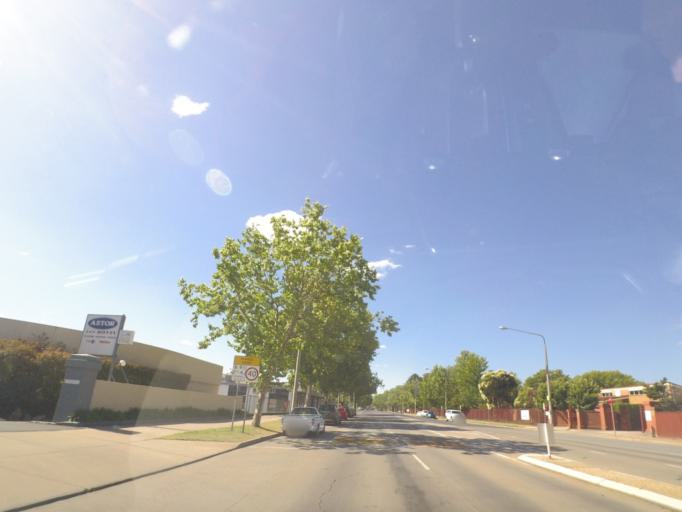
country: AU
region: New South Wales
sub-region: Albury Municipality
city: Albury
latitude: -36.0746
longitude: 146.9253
